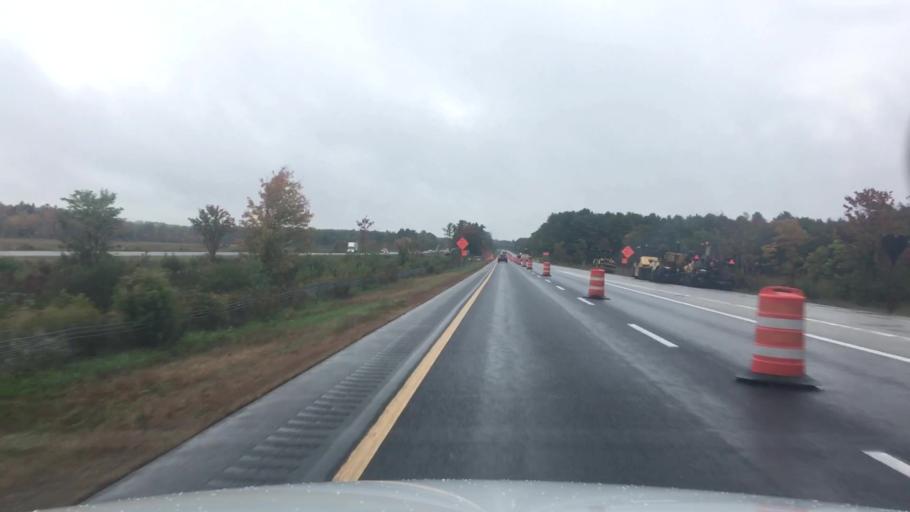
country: US
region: Maine
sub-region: Sagadahoc County
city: Richmond
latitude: 44.1044
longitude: -69.8656
